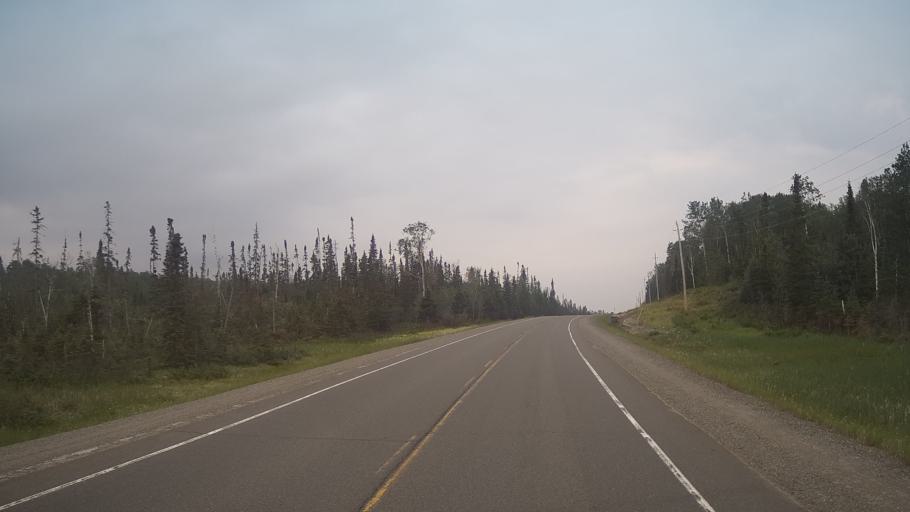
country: CA
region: Ontario
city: Greenstone
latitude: 49.5205
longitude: -88.0239
